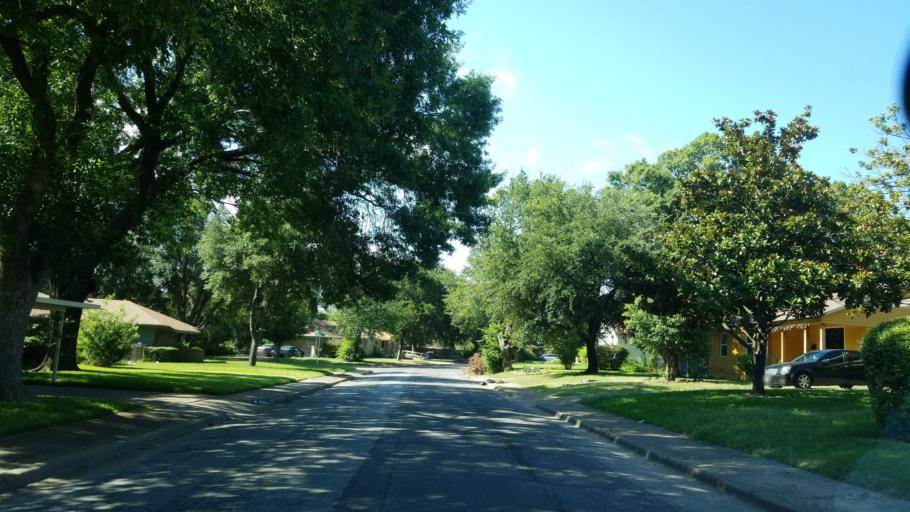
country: US
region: Texas
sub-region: Dallas County
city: Dallas
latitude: 32.7168
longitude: -96.8032
